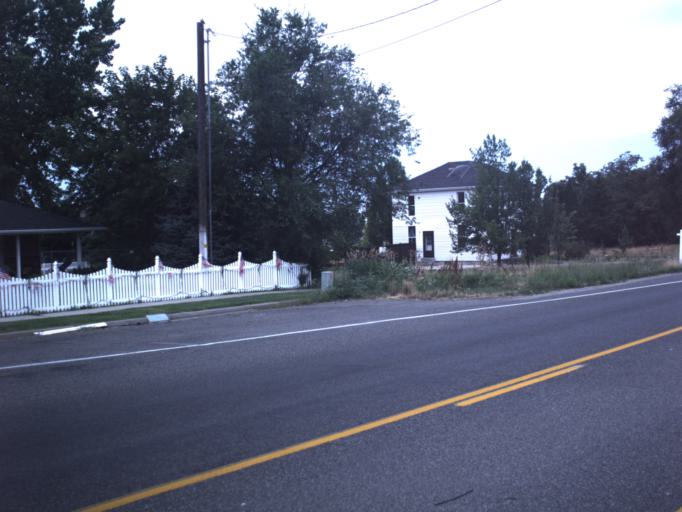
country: US
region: Utah
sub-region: Weber County
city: West Haven
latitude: 41.1730
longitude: -112.0644
